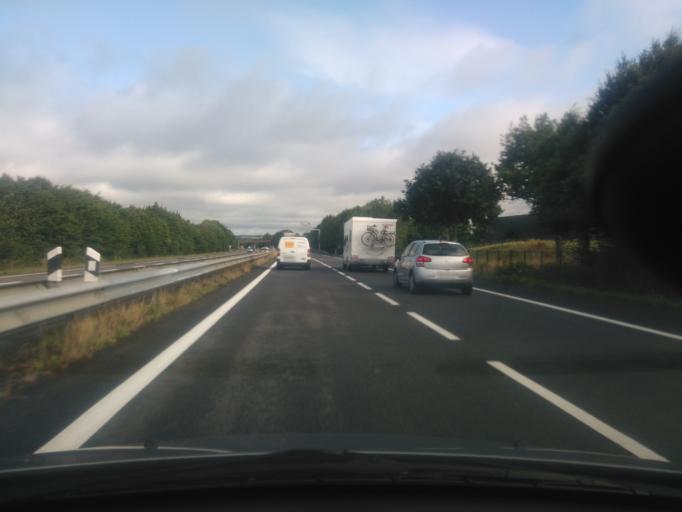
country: FR
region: Brittany
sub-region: Departement d'Ille-et-Vilaine
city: Saint-Domineuc
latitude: 48.3611
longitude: -1.8720
